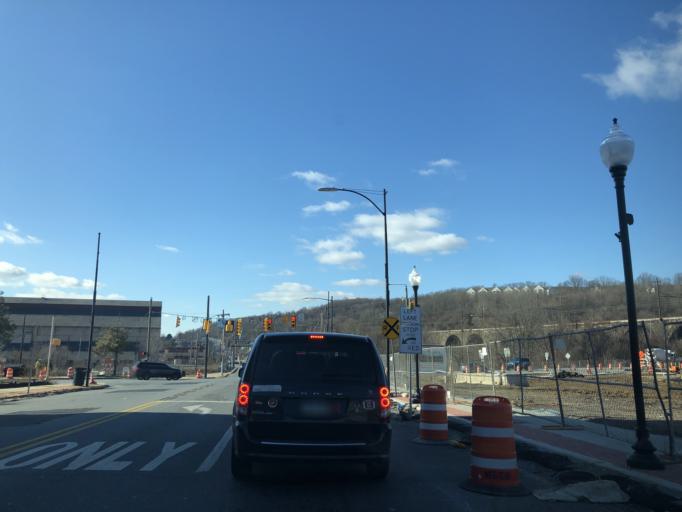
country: US
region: Pennsylvania
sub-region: Chester County
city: Coatesville
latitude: 39.9832
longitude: -75.8230
